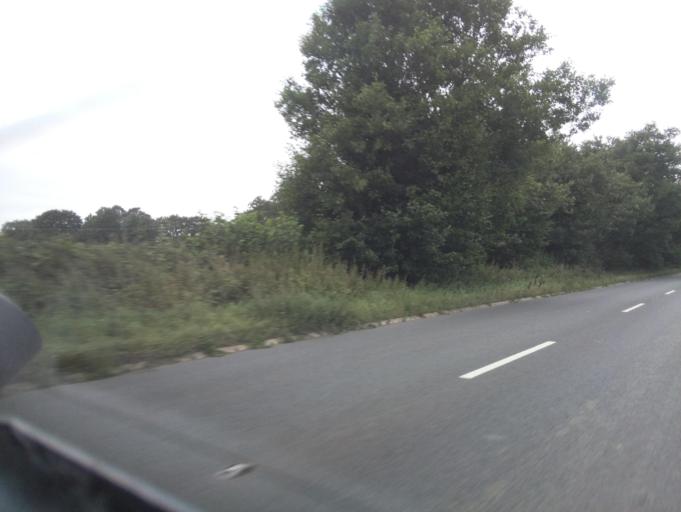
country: GB
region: England
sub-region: Shropshire
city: Shawbury
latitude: 52.8129
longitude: -2.6139
